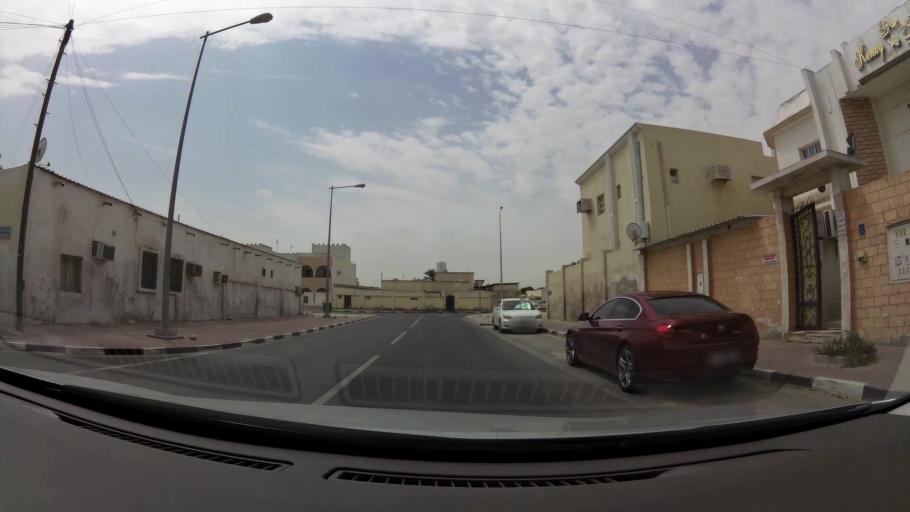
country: QA
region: Baladiyat ar Rayyan
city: Ar Rayyan
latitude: 25.3317
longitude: 51.4735
